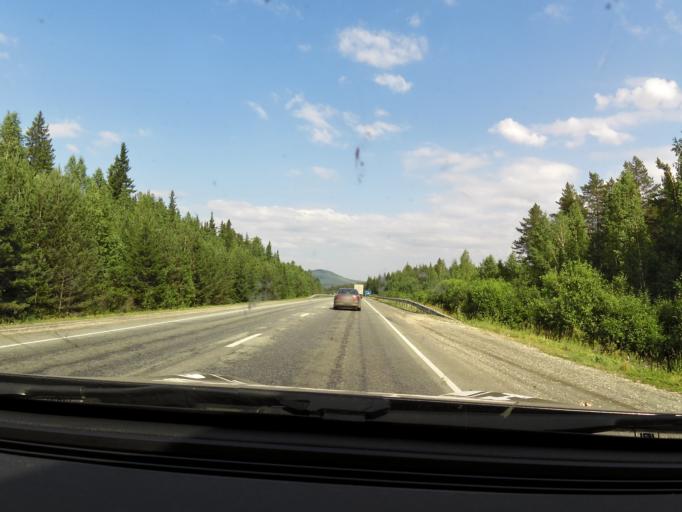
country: RU
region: Sverdlovsk
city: Revda
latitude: 56.8267
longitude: 59.9135
